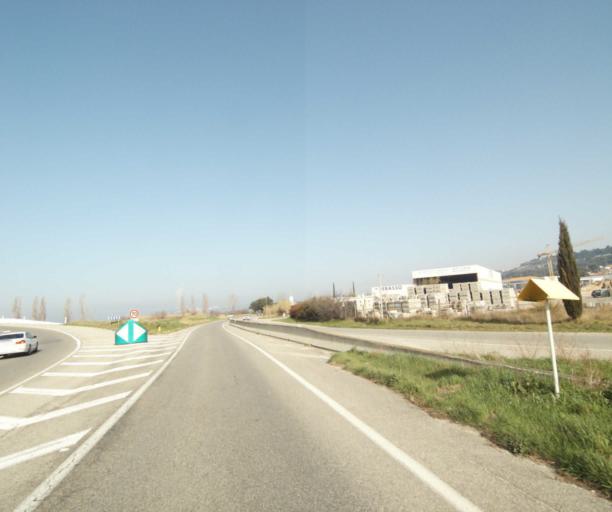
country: FR
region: Provence-Alpes-Cote d'Azur
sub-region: Departement des Bouches-du-Rhone
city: Vitrolles
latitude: 43.4454
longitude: 5.2310
